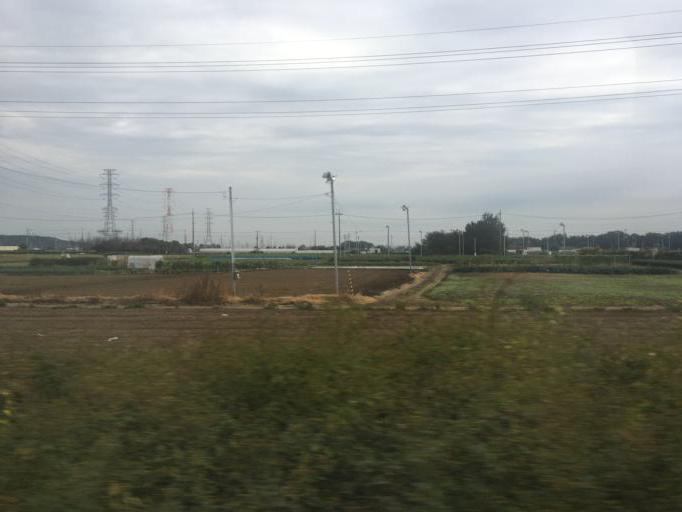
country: JP
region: Saitama
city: Hanno
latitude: 35.8049
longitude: 139.3318
